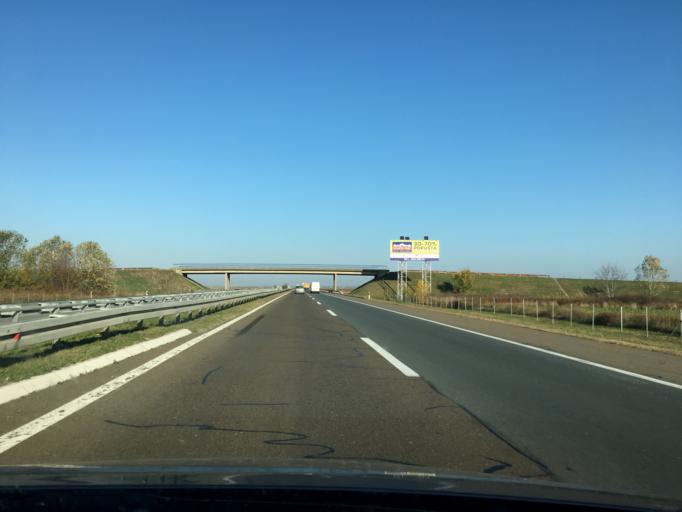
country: RS
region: Autonomna Pokrajina Vojvodina
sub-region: Sremski Okrug
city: Stara Pazova
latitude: 45.0264
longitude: 20.1902
